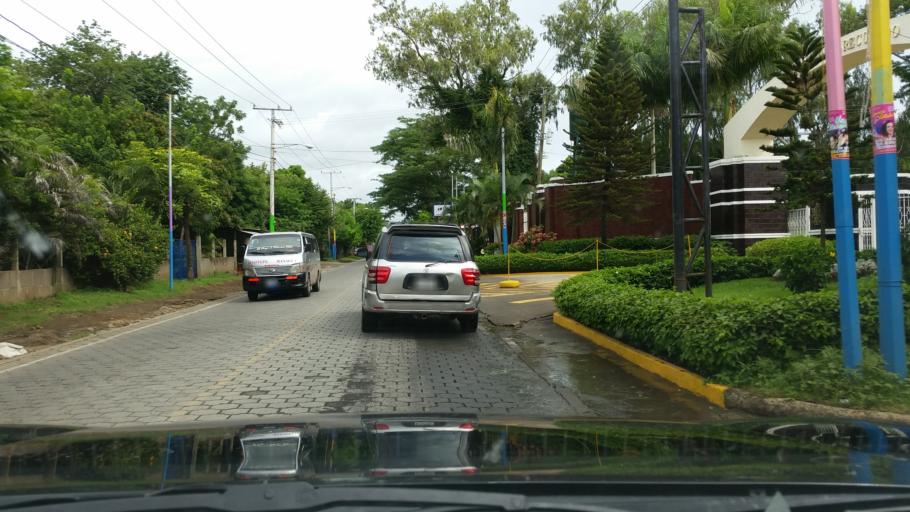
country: NI
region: Masaya
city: Ticuantepe
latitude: 12.0515
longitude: -86.2029
